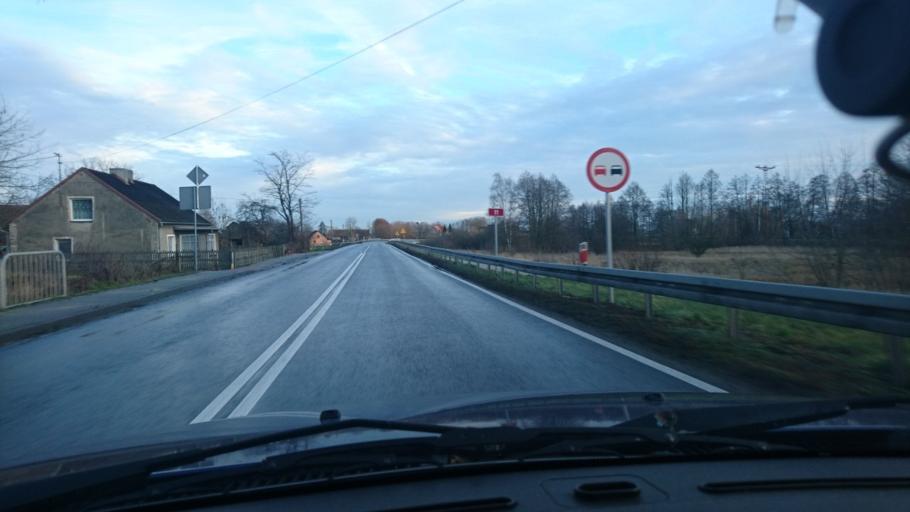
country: PL
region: Greater Poland Voivodeship
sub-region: Powiat kepinski
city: Opatow
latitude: 51.1652
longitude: 18.1483
